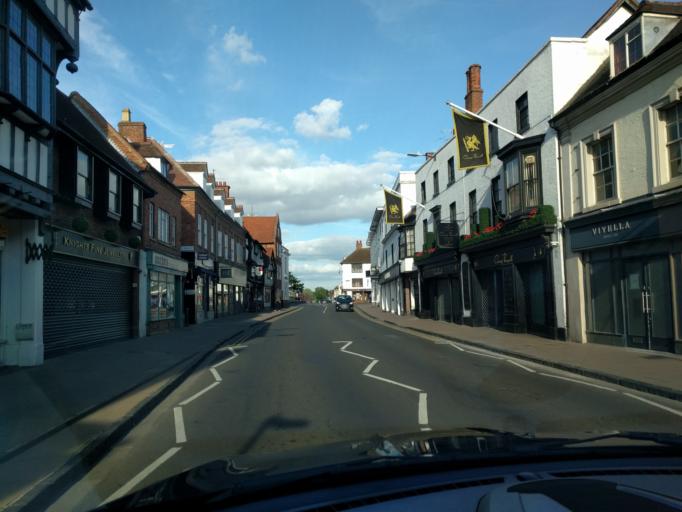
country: GB
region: England
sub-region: Warwickshire
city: Stratford-upon-Avon
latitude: 52.1928
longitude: -1.7076
